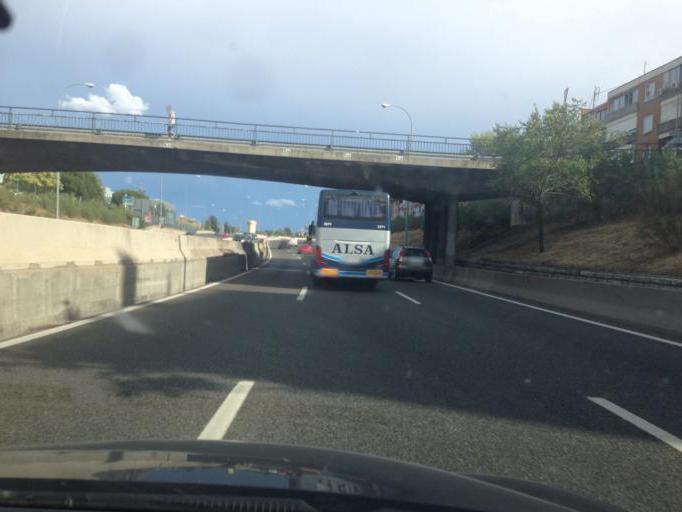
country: ES
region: Madrid
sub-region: Provincia de Madrid
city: Las Rozas de Madrid
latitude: 40.4919
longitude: -3.8678
